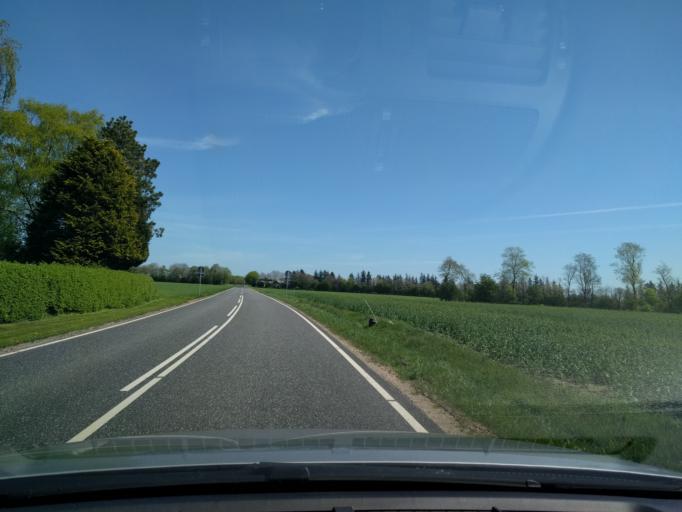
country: DK
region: South Denmark
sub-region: Billund Kommune
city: Billund
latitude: 55.6790
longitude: 9.0054
